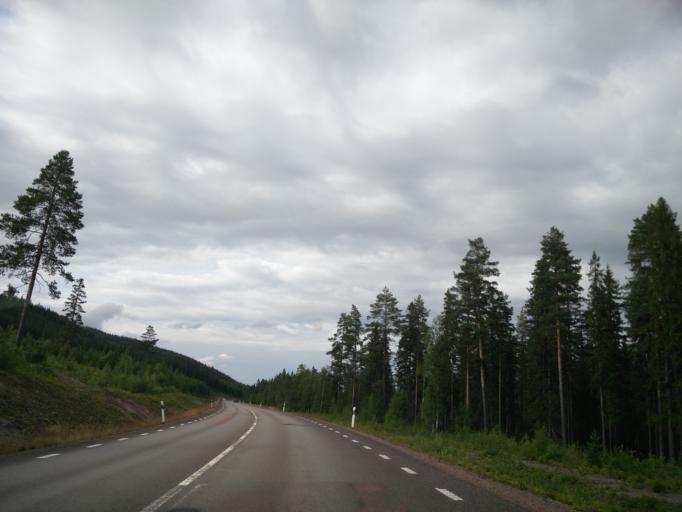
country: SE
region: Dalarna
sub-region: Malung-Saelens kommun
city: Malung
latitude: 60.6155
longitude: 13.6076
